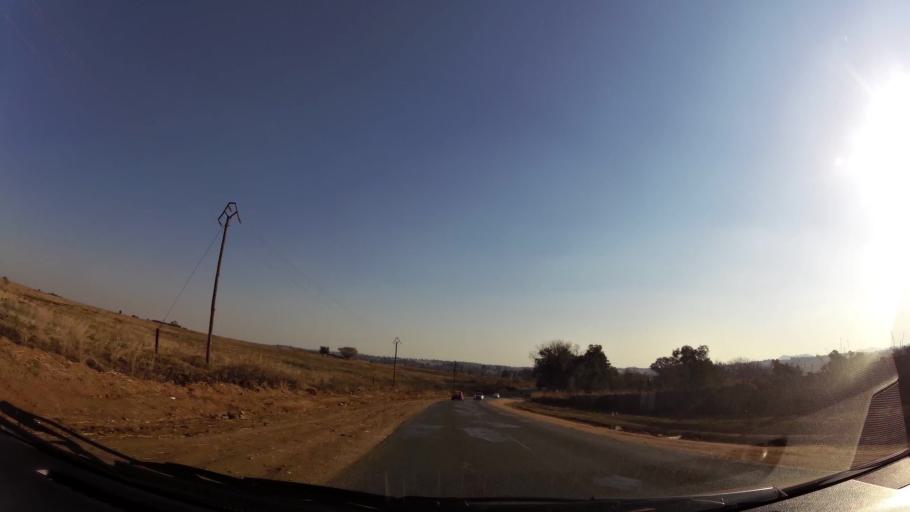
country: ZA
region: Gauteng
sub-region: West Rand District Municipality
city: Muldersdriseloop
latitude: -26.0045
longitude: 27.9166
